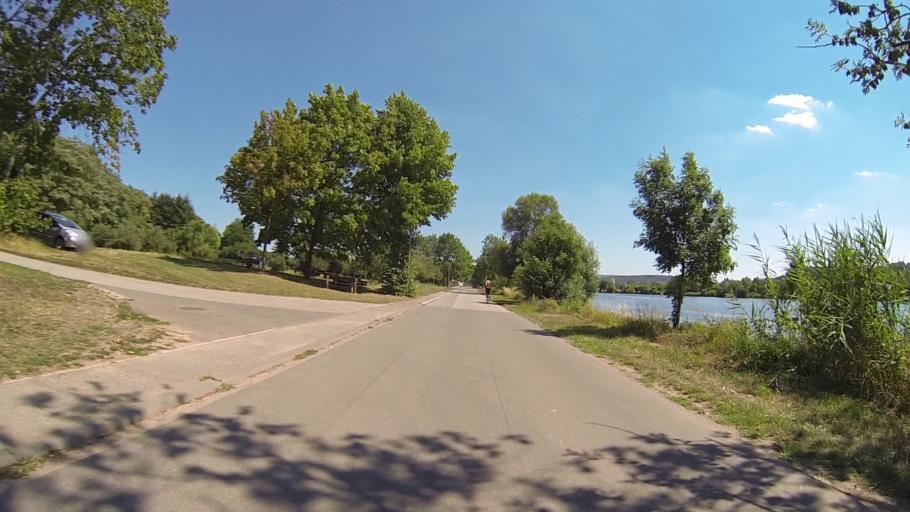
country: DE
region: Rheinland-Pfalz
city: Wasserliesch
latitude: 49.7065
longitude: 6.5507
